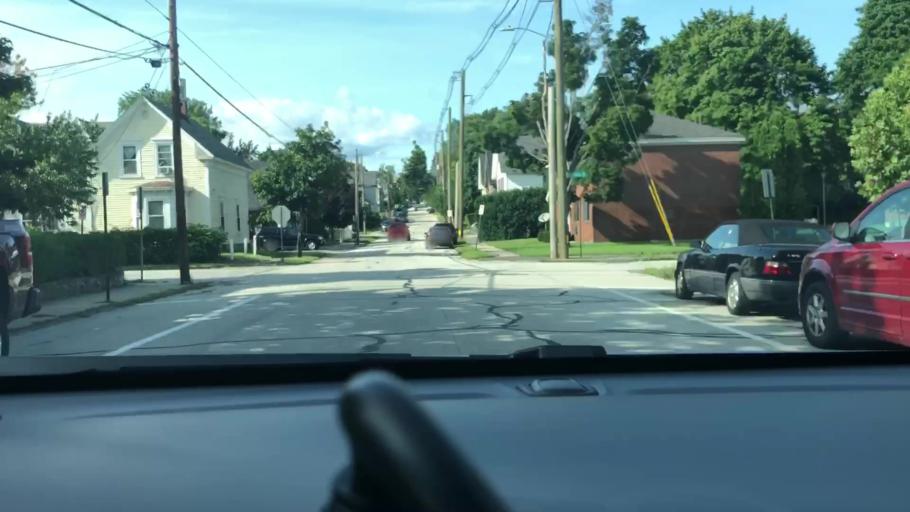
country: US
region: New Hampshire
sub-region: Hillsborough County
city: Manchester
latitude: 42.9878
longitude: -71.4463
